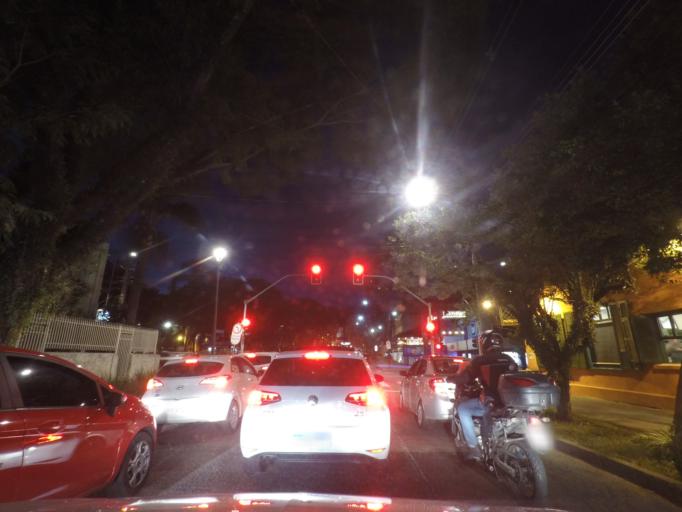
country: BR
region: Parana
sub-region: Curitiba
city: Curitiba
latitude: -25.4357
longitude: -49.2862
